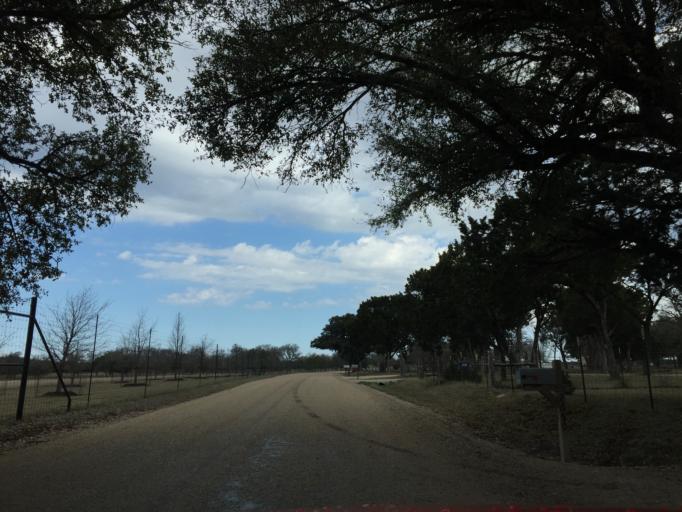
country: US
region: Texas
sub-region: Burnet County
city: Bertram
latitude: 30.6445
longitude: -98.0125
